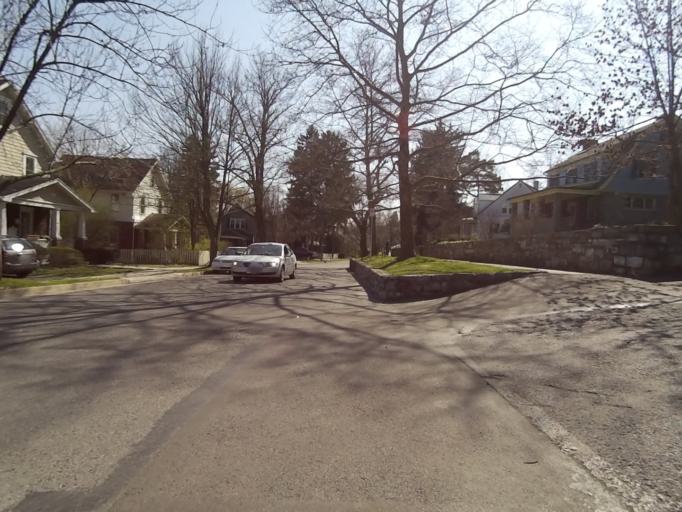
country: US
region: Pennsylvania
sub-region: Centre County
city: State College
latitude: 40.7902
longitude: -77.8557
